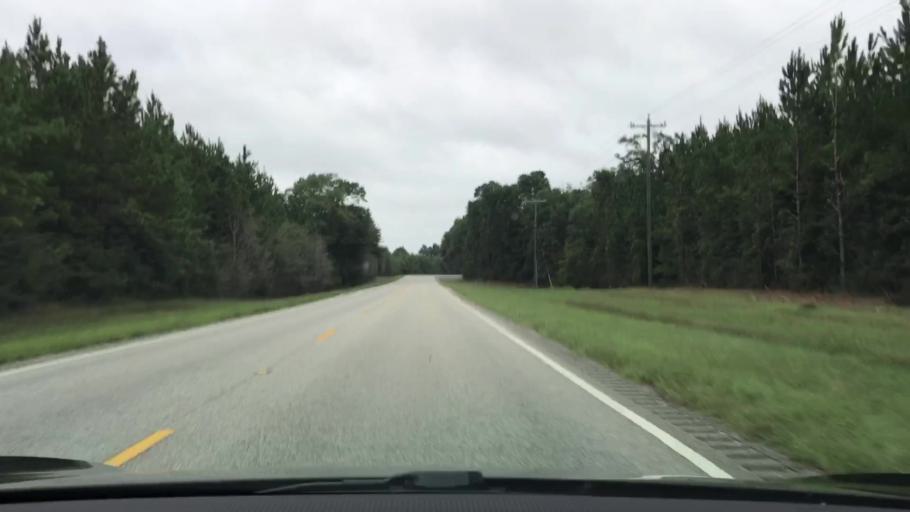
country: US
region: Alabama
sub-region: Coffee County
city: Elba
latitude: 31.3759
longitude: -86.0922
